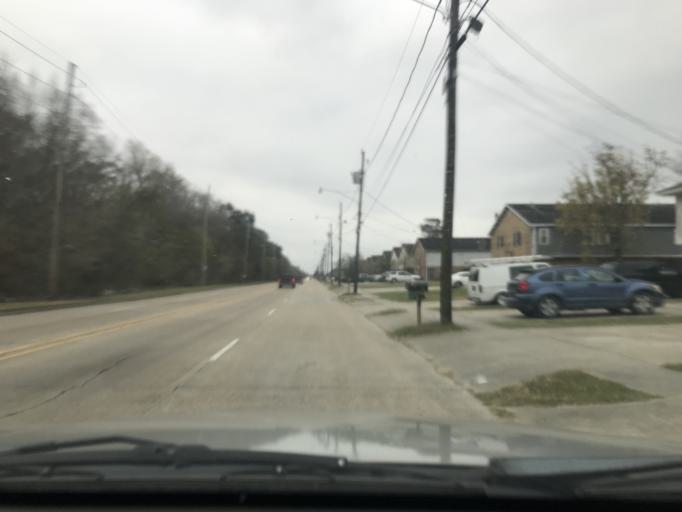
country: US
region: Louisiana
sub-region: Jefferson Parish
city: Woodmere
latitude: 29.8670
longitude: -90.0748
